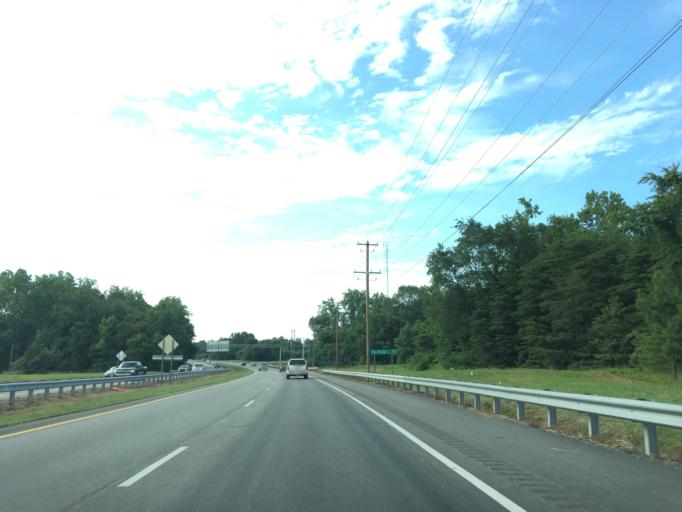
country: US
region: Maryland
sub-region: Queen Anne's County
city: Centreville
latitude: 38.9432
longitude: -76.0627
